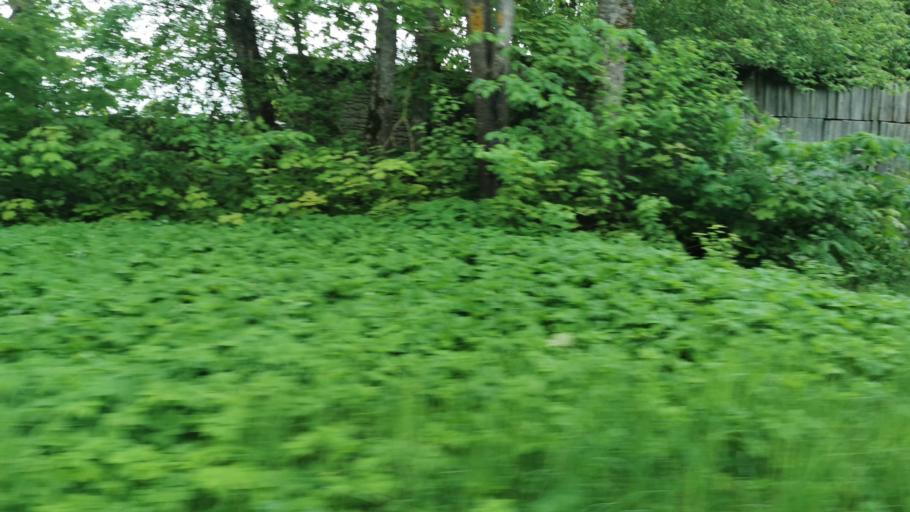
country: EE
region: Laeaene-Virumaa
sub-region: Vinni vald
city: Vinni
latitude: 59.2675
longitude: 26.3648
